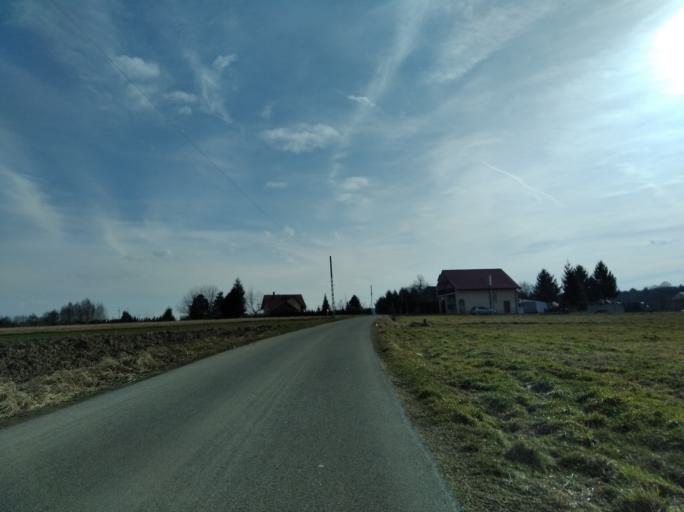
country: PL
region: Subcarpathian Voivodeship
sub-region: Powiat brzozowski
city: Grabownica Starzenska
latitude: 49.6502
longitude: 22.0702
